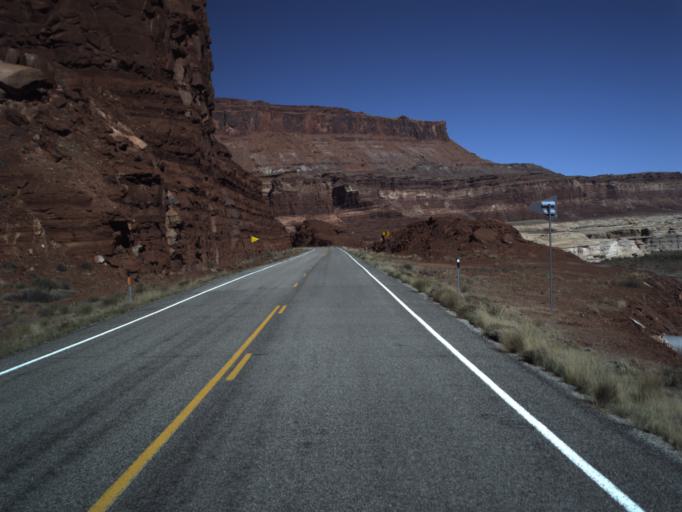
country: US
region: Utah
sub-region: San Juan County
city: Blanding
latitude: 37.8959
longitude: -110.3981
